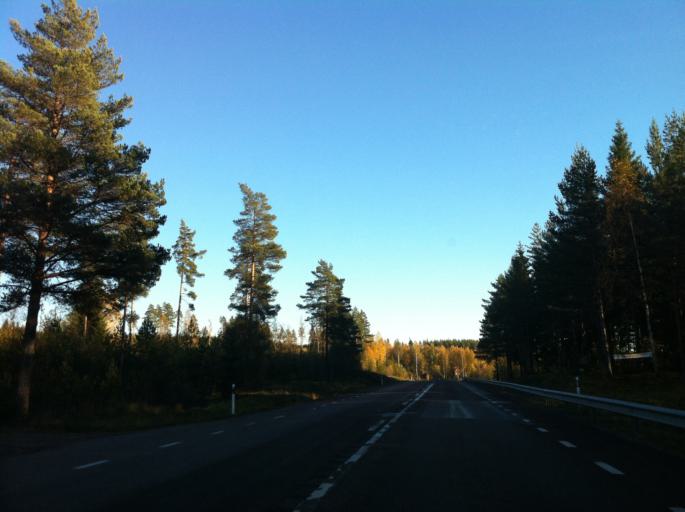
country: SE
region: Dalarna
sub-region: Faluns Kommun
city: Grycksbo
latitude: 60.7024
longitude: 15.4722
